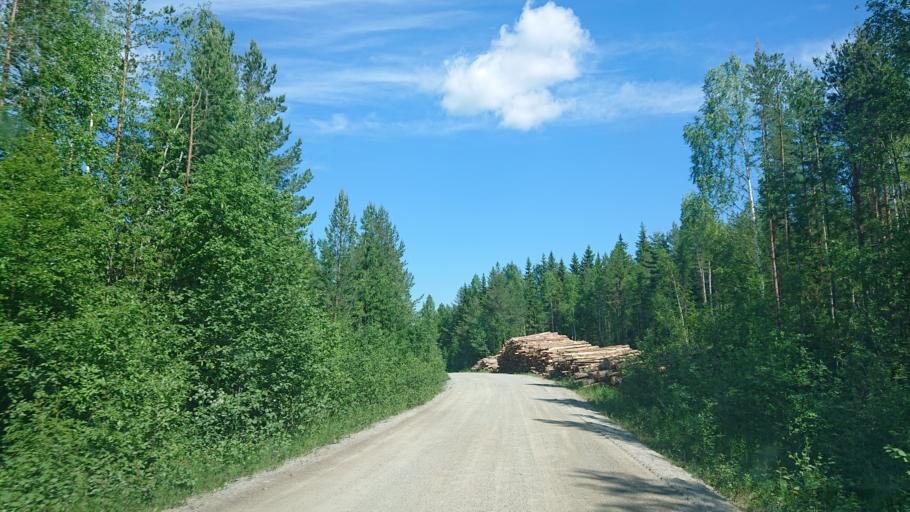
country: SE
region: Vaesternorrland
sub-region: Solleftea Kommun
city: Solleftea
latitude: 62.9679
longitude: 17.1575
